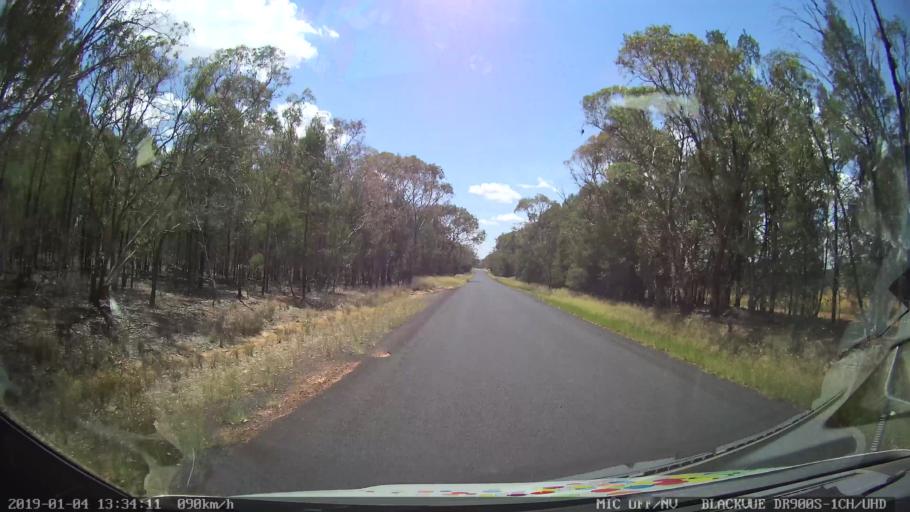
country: AU
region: New South Wales
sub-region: Dubbo Municipality
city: Dubbo
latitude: -32.5890
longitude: 148.5372
